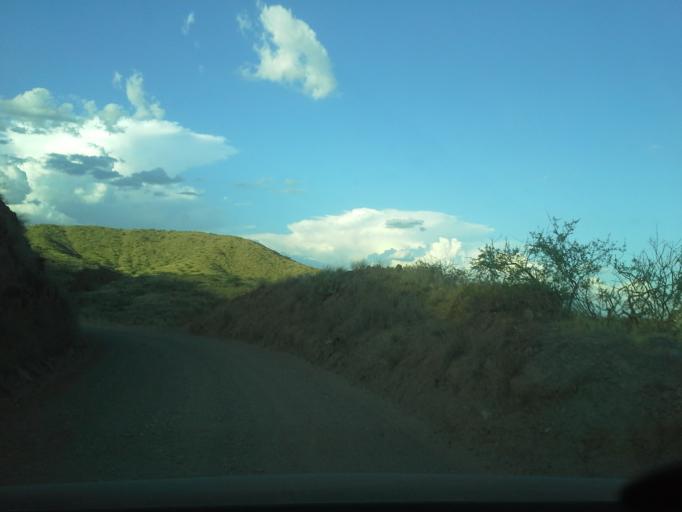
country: US
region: Arizona
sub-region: Yavapai County
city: Spring Valley
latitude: 34.2754
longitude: -112.2444
